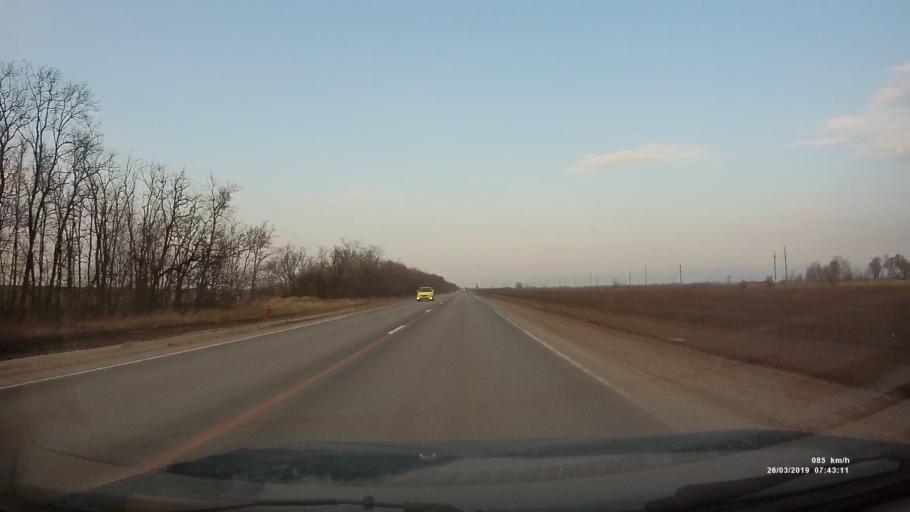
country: RU
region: Rostov
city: Novobessergenovka
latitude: 47.1832
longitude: 38.5992
